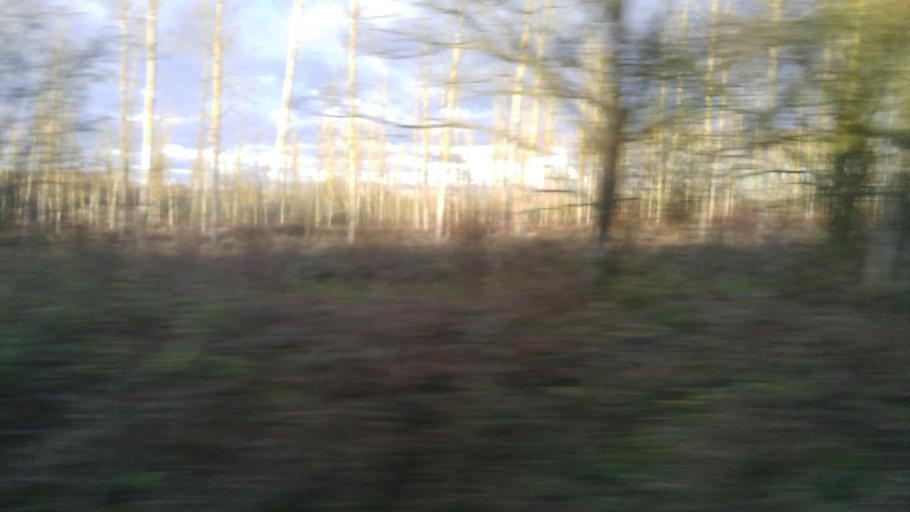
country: GB
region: England
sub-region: Kent
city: Headcorn
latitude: 51.1605
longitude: 0.6957
